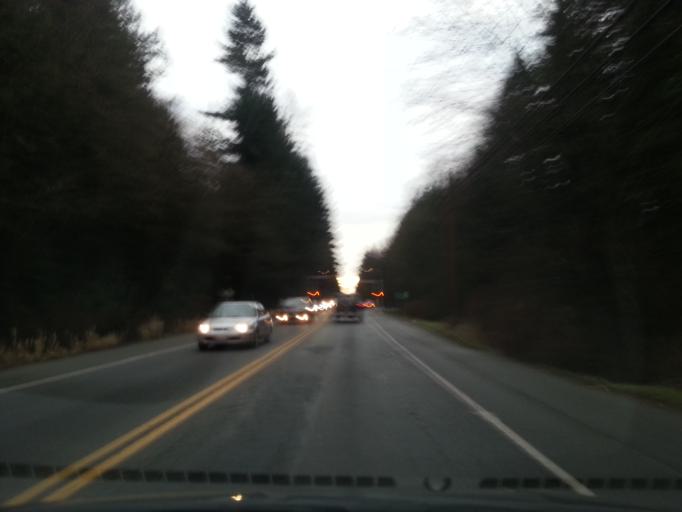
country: CA
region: British Columbia
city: Surrey
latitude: 49.1752
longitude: -122.8250
